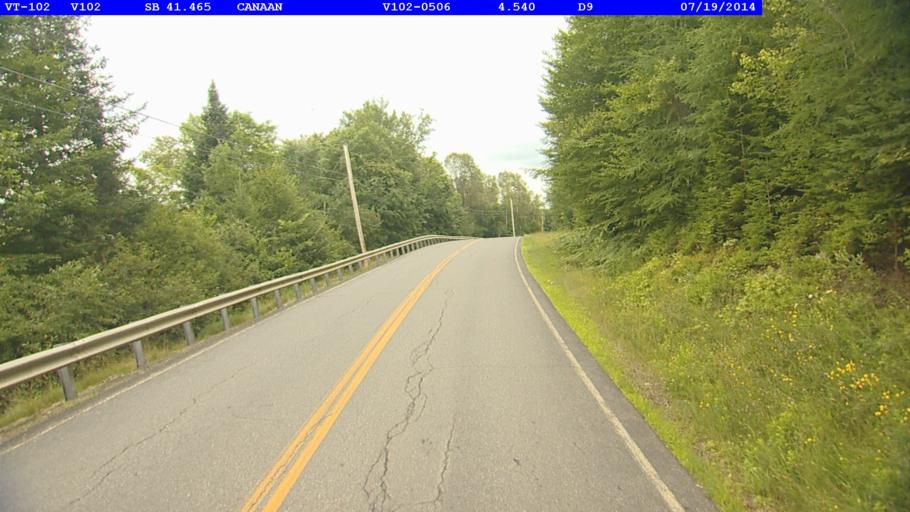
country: US
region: New Hampshire
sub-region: Coos County
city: Colebrook
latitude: 44.9698
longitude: -71.5264
